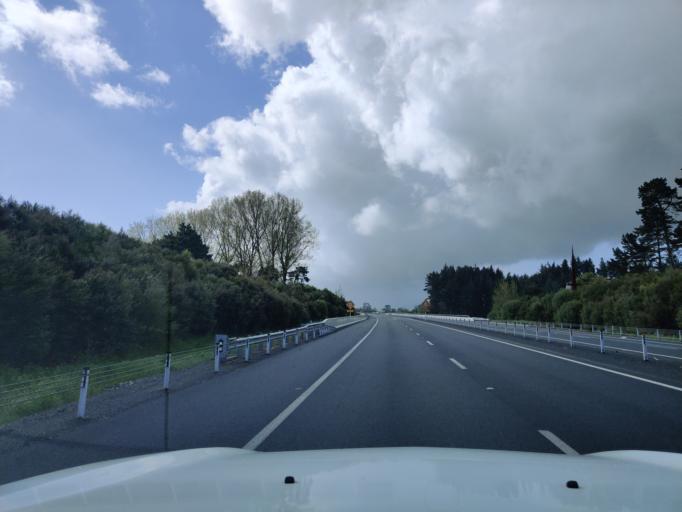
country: NZ
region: Waikato
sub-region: Waipa District
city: Cambridge
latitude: -37.8867
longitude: 175.4945
